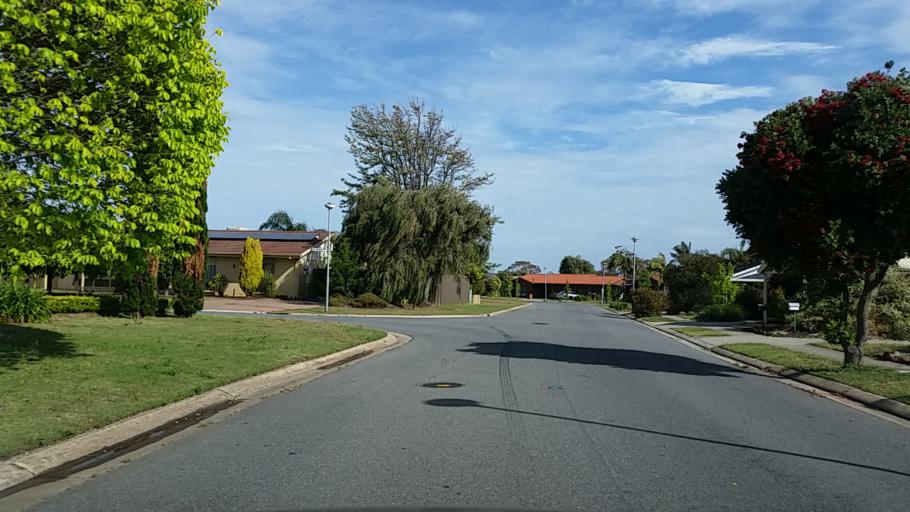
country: AU
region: South Australia
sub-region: Charles Sturt
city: Grange
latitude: -34.8957
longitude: 138.4966
